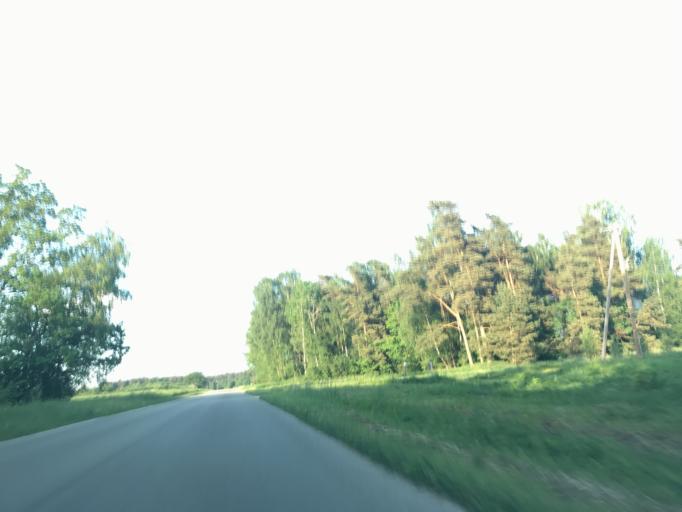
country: LV
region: Lecava
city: Iecava
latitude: 56.6175
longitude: 24.2492
